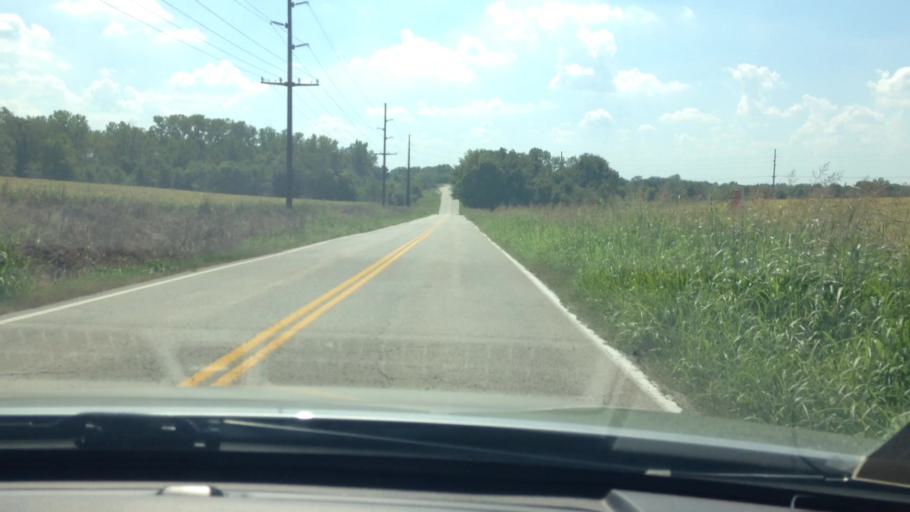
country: US
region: Missouri
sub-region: Platte County
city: Platte City
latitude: 39.3441
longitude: -94.7330
